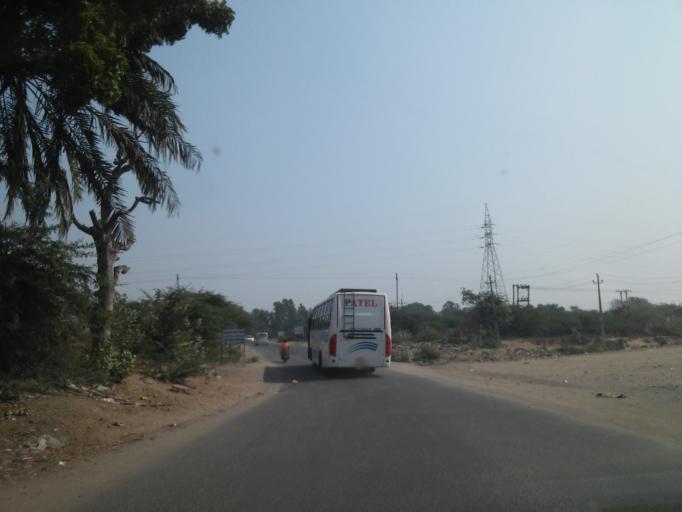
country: IN
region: Gujarat
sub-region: Kachchh
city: Mundra
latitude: 22.8403
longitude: 69.7085
